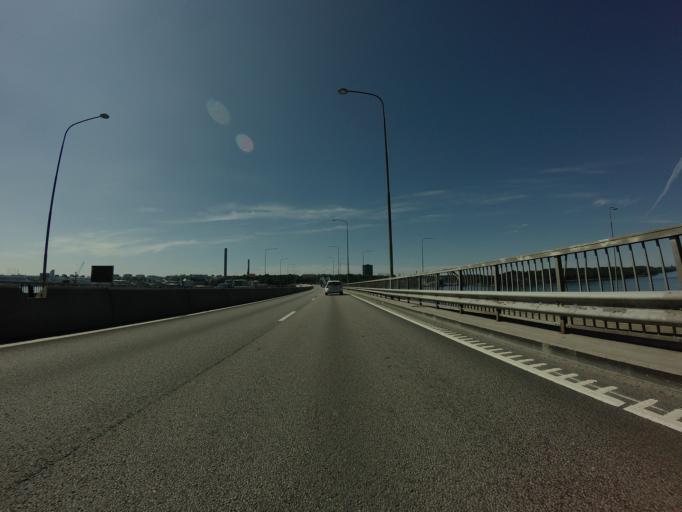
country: SE
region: Stockholm
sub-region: Lidingo
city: Lidingoe
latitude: 59.3625
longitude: 18.1152
